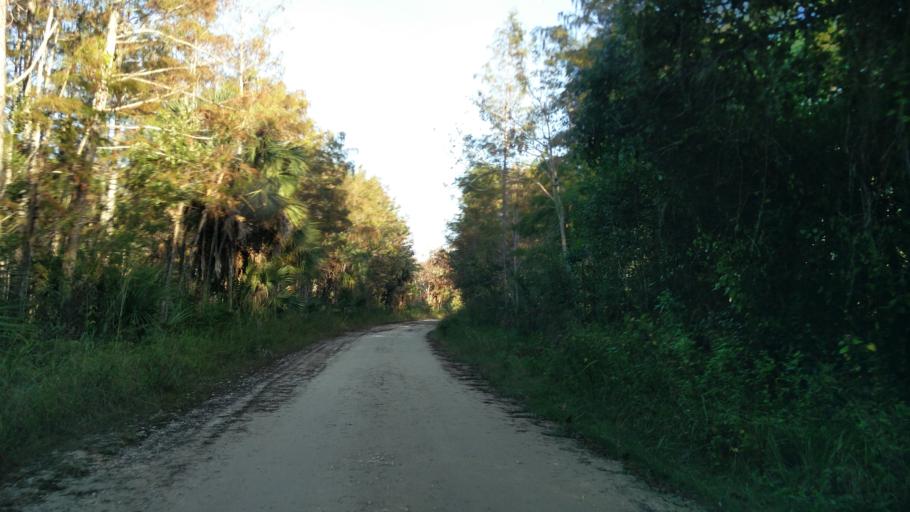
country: US
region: Florida
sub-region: Collier County
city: Lely Resort
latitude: 25.9801
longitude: -81.3739
